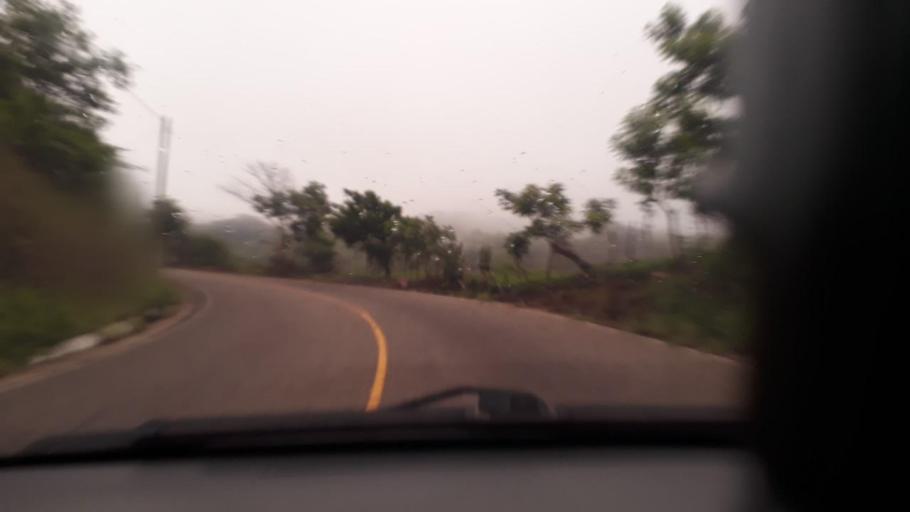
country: GT
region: Jutiapa
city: Jalpatagua
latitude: 14.1792
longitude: -90.0432
